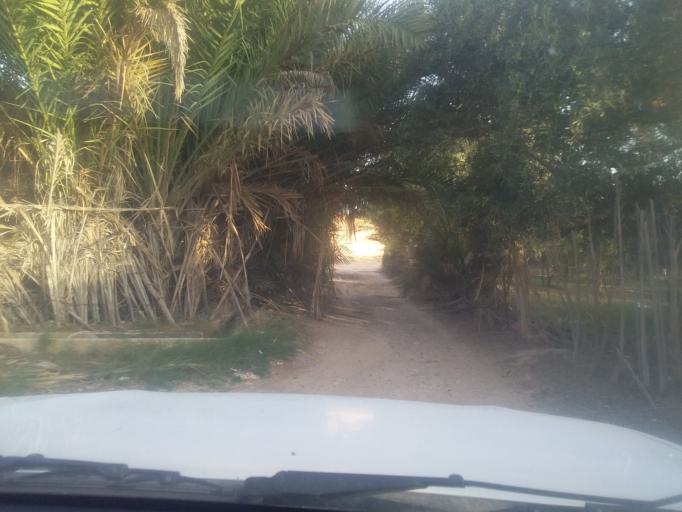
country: TN
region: Qabis
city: Gabes
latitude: 33.6297
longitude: 10.2957
